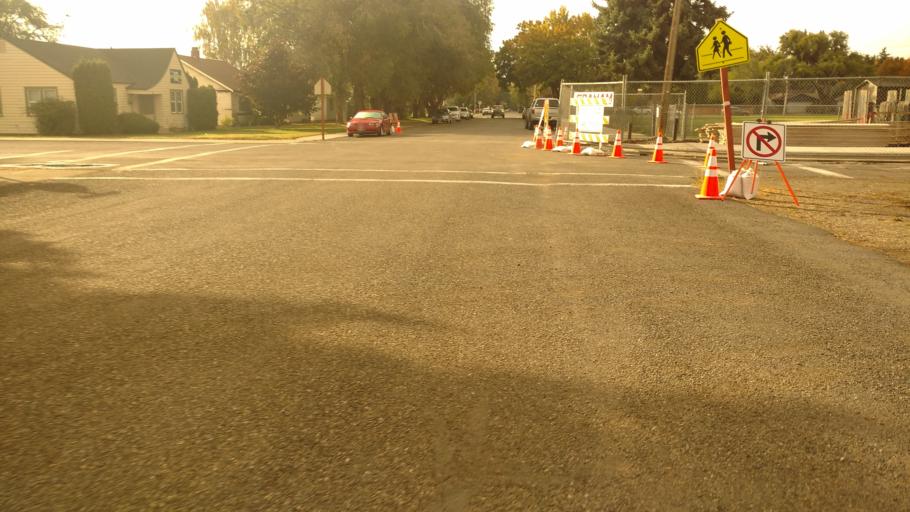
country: US
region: Washington
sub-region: Kittitas County
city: Ellensburg
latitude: 46.9928
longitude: -120.5404
